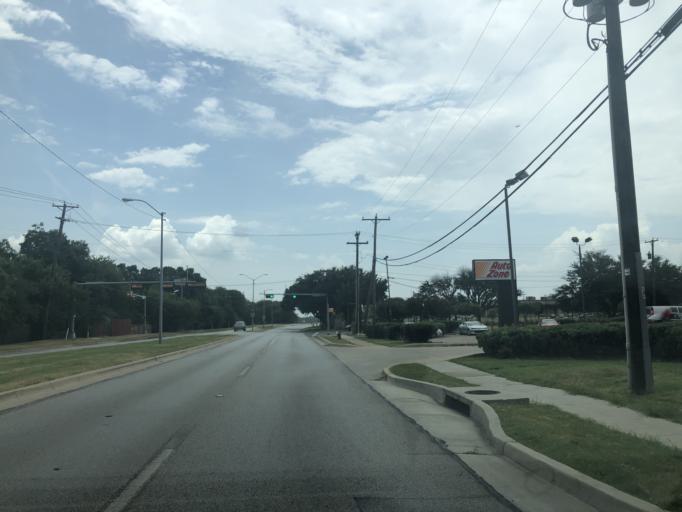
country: US
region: Texas
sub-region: Dallas County
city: Grand Prairie
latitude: 32.7387
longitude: -97.0144
